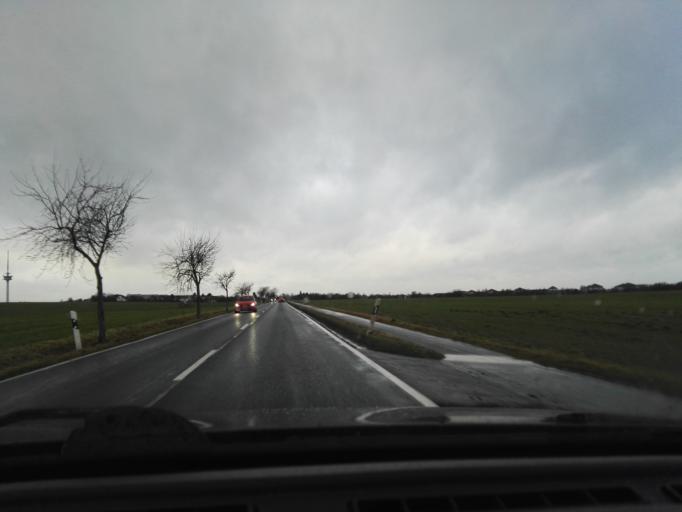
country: DE
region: Lower Saxony
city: Leiferde
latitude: 52.2281
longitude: 10.4999
